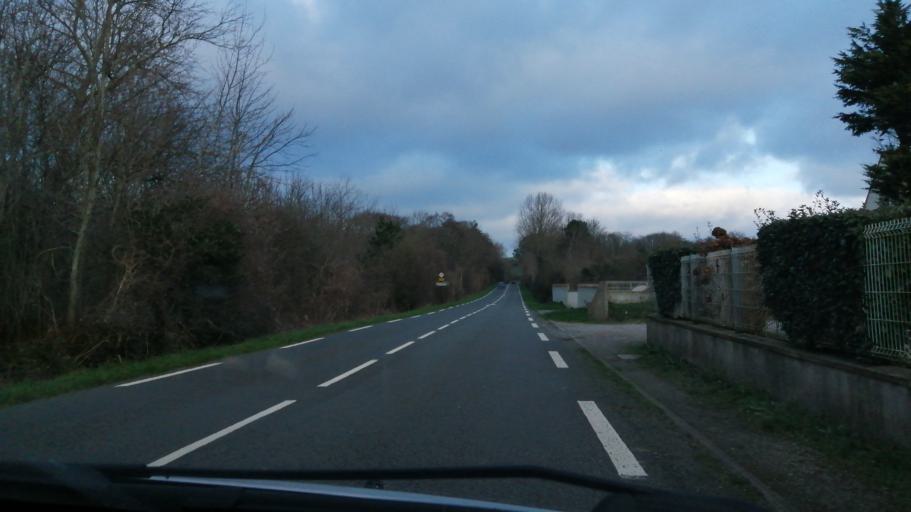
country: FR
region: Nord-Pas-de-Calais
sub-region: Departement du Pas-de-Calais
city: Wissant
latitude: 50.8903
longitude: 1.6788
